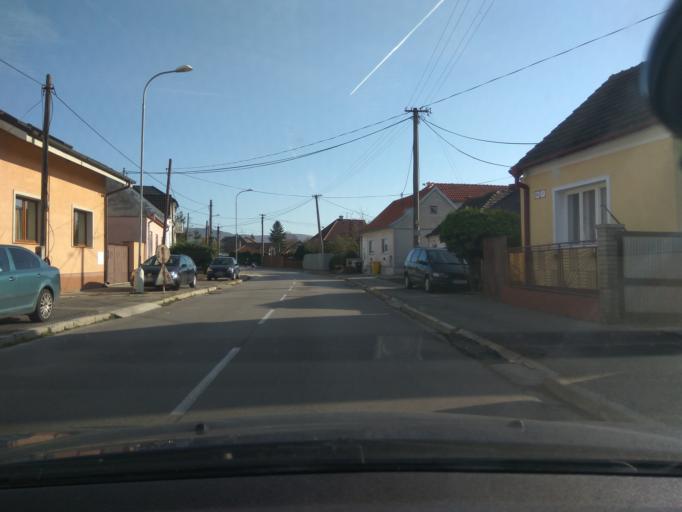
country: SK
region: Trnavsky
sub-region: Okres Trnava
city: Piestany
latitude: 48.6056
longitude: 17.8250
